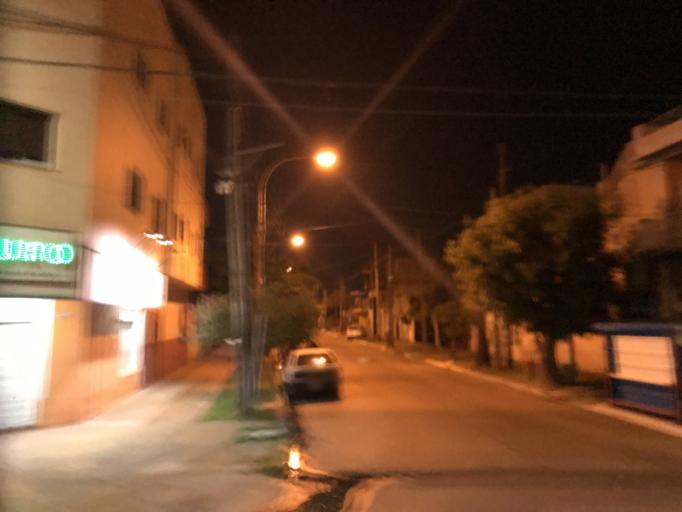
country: AR
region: Buenos Aires
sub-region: Partido de Lanus
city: Lanus
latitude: -34.6915
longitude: -58.4134
